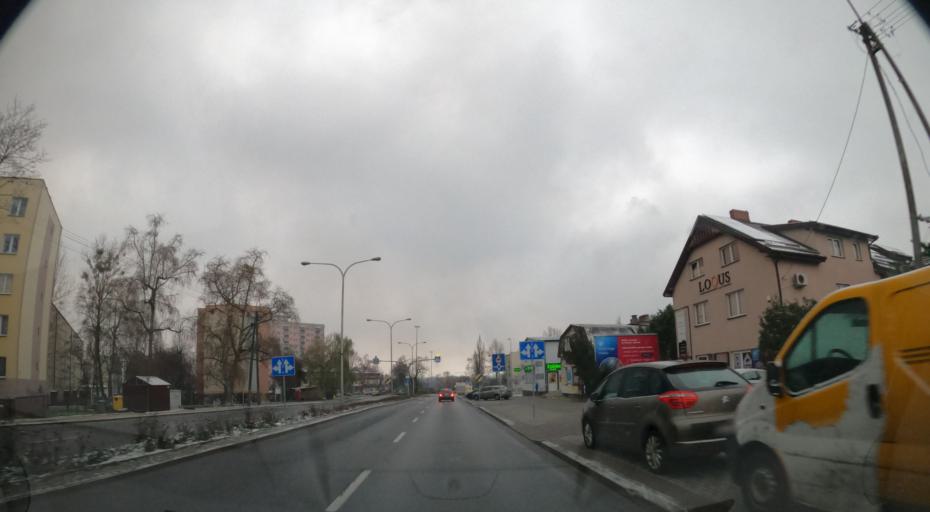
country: PL
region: Masovian Voivodeship
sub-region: Plock
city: Plock
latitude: 52.5565
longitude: 19.6693
